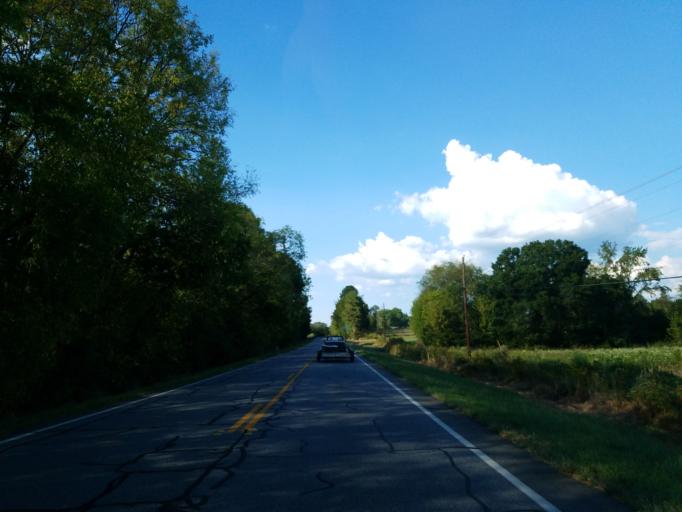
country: US
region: Georgia
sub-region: Murray County
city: Chatsworth
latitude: 34.5553
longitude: -84.7076
